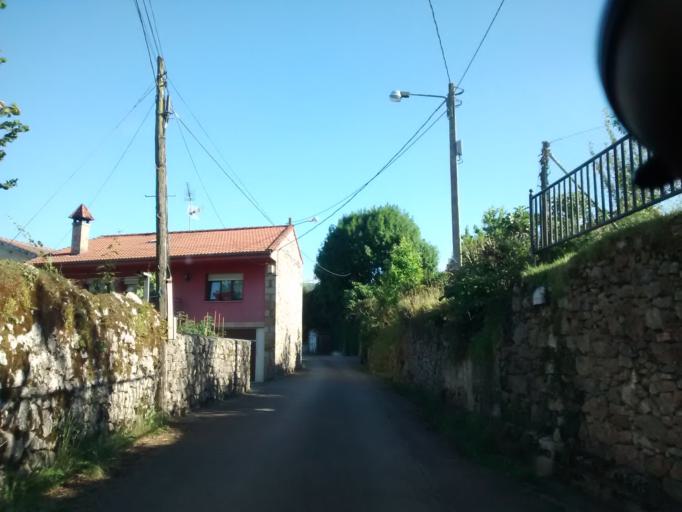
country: ES
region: Cantabria
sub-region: Provincia de Cantabria
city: Entrambasaguas
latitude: 43.3646
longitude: -3.7009
